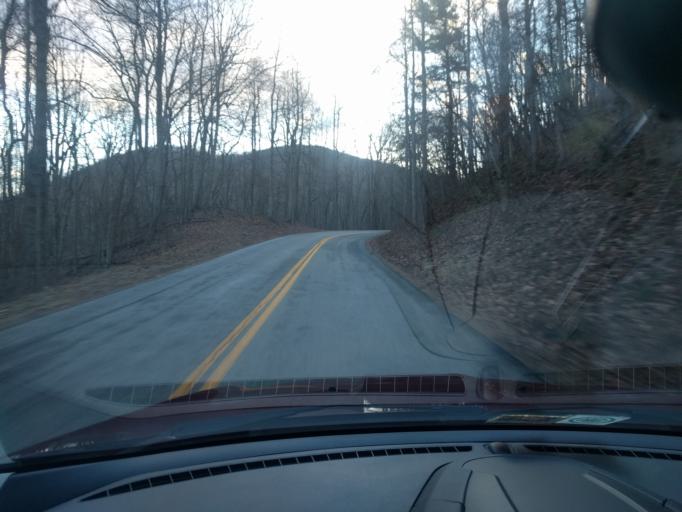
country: US
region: Virginia
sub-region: Botetourt County
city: Buchanan
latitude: 37.4625
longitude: -79.6351
